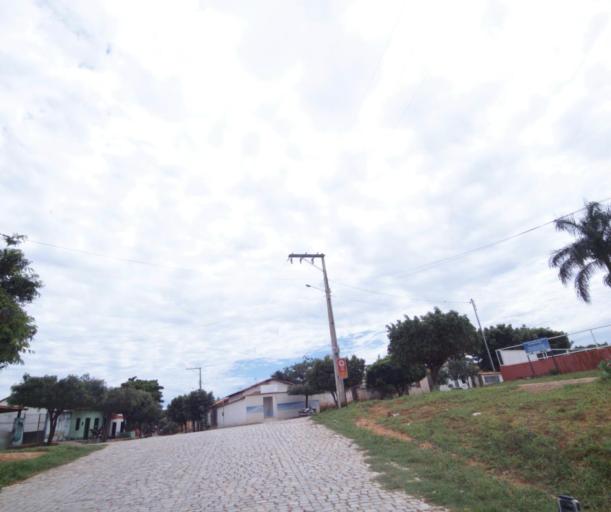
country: BR
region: Bahia
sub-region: Carinhanha
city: Carinhanha
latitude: -14.2146
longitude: -44.2841
